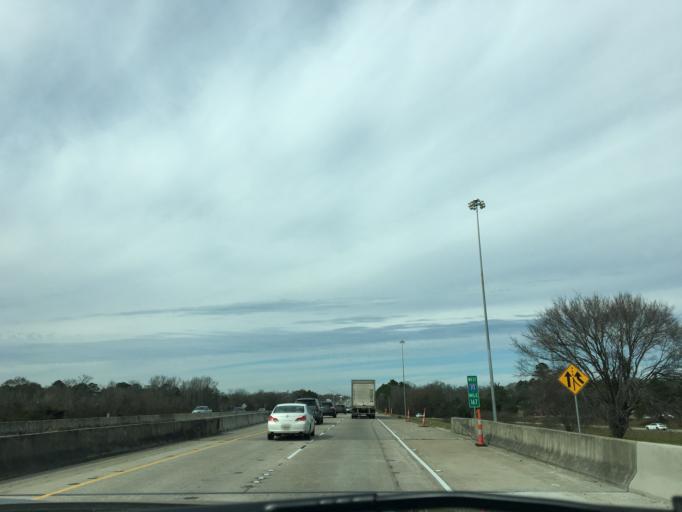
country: US
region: Louisiana
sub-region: East Baton Rouge Parish
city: Old Jefferson
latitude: 30.3465
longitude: -91.0295
